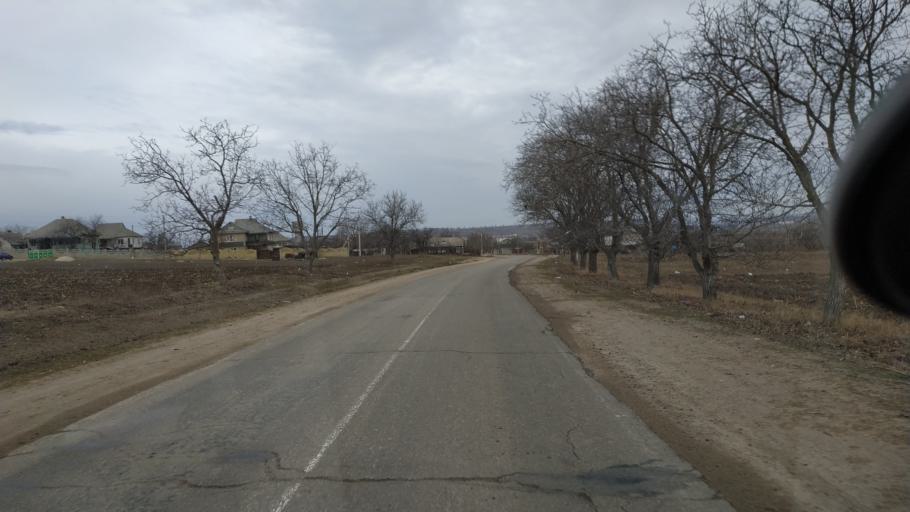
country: MD
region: Telenesti
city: Dubasari
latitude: 47.2446
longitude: 29.1421
